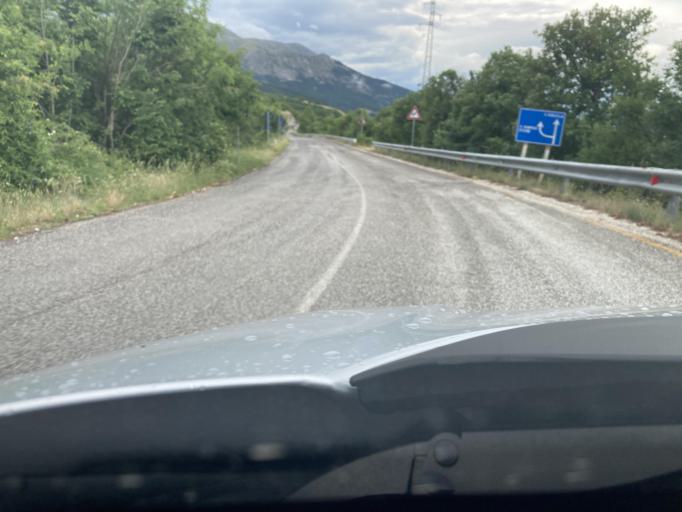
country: IT
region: Abruzzo
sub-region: Provincia dell' Aquila
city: San Panfilo d'Ocre
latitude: 42.2737
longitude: 13.4853
